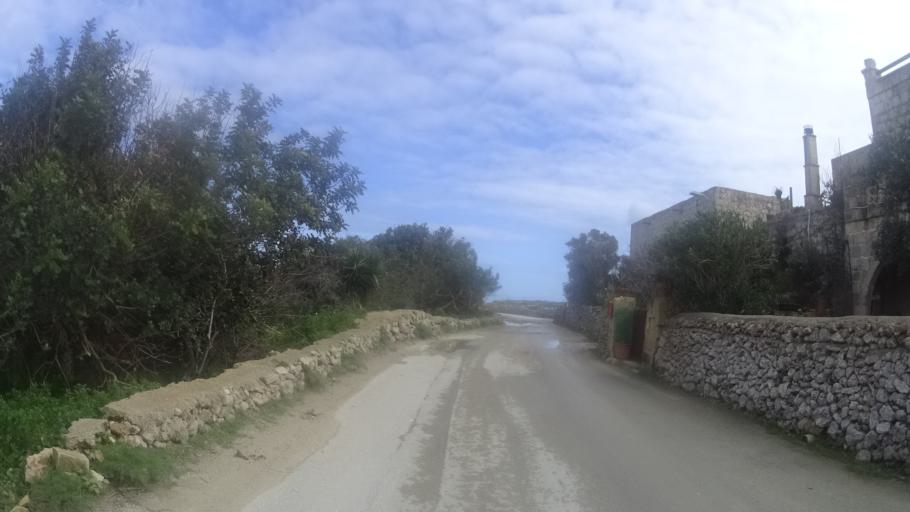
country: MT
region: Il-Qala
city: Qala
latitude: 36.0422
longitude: 14.3134
